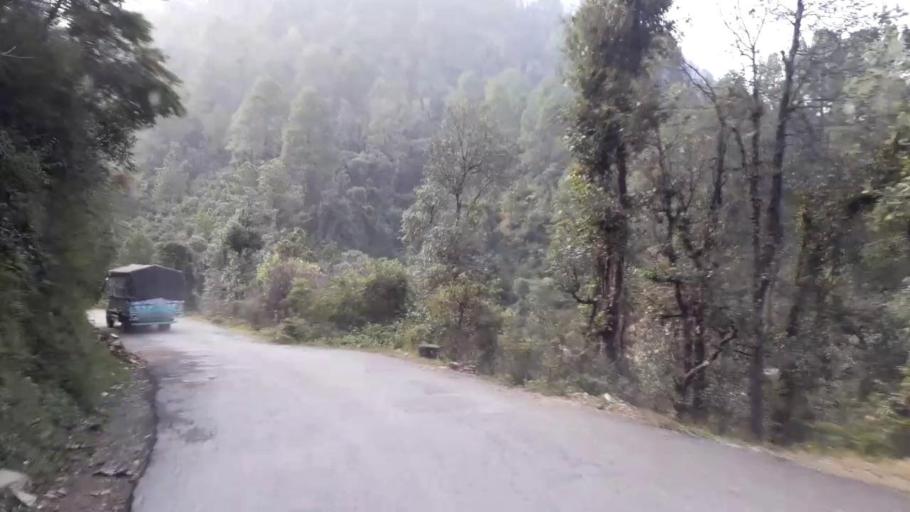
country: IN
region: Himachal Pradesh
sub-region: Shimla
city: Shimla
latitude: 31.0502
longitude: 77.1490
